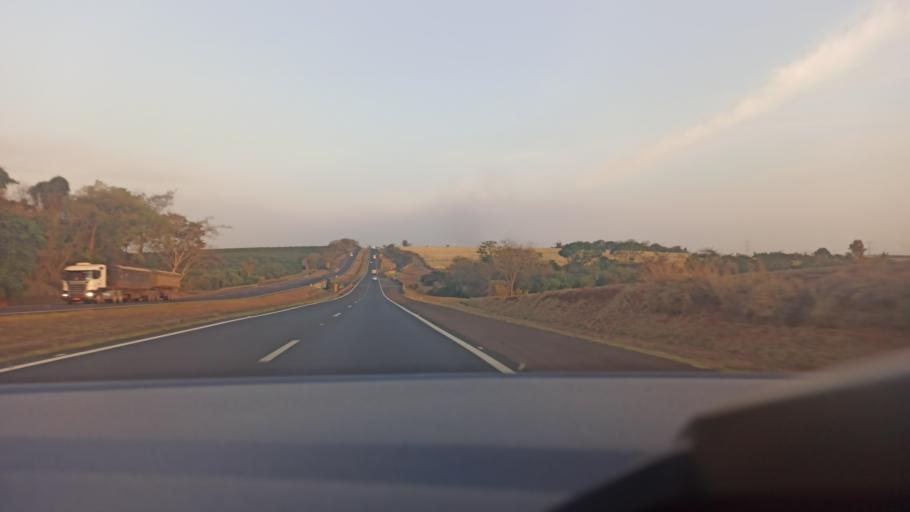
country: BR
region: Sao Paulo
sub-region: Taquaritinga
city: Taquaritinga
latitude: -21.4325
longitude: -48.6611
